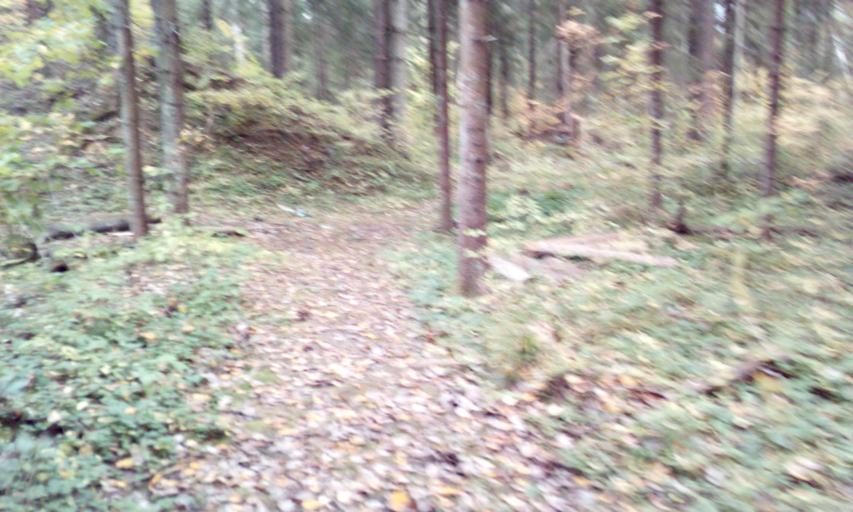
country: RU
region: Moskovskaya
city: Selyatino
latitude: 55.4840
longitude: 36.9608
